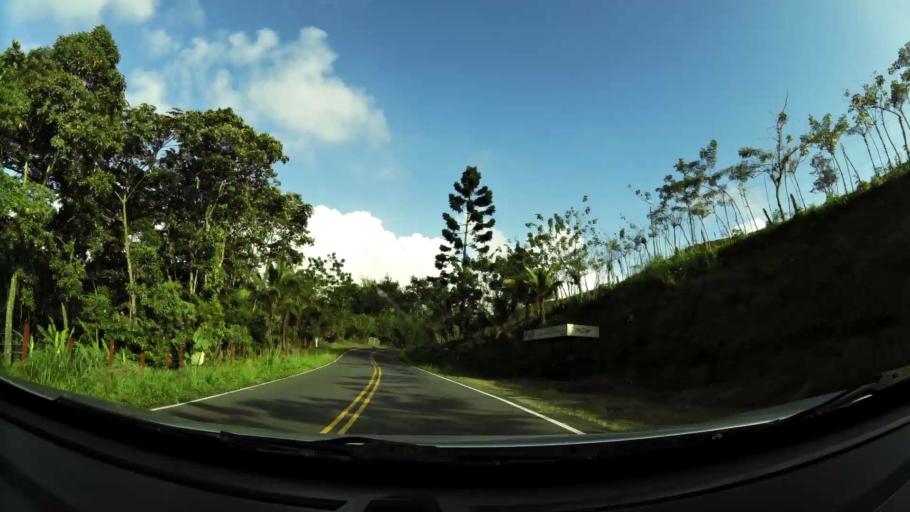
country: CR
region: Limon
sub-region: Canton de Siquirres
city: Siquirres
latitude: 10.0547
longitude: -83.5522
